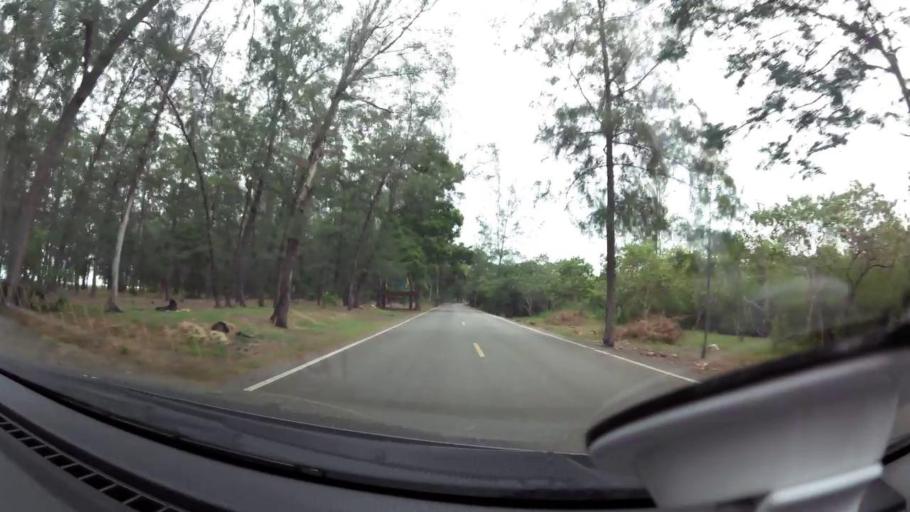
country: TH
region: Prachuap Khiri Khan
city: Pran Buri
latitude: 12.4175
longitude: 99.9843
